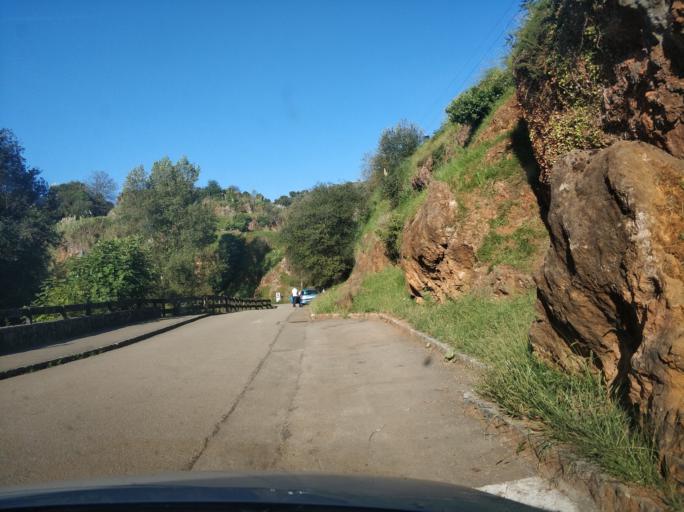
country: ES
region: Cantabria
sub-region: Provincia de Cantabria
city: Penagos
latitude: 43.3598
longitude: -3.8293
